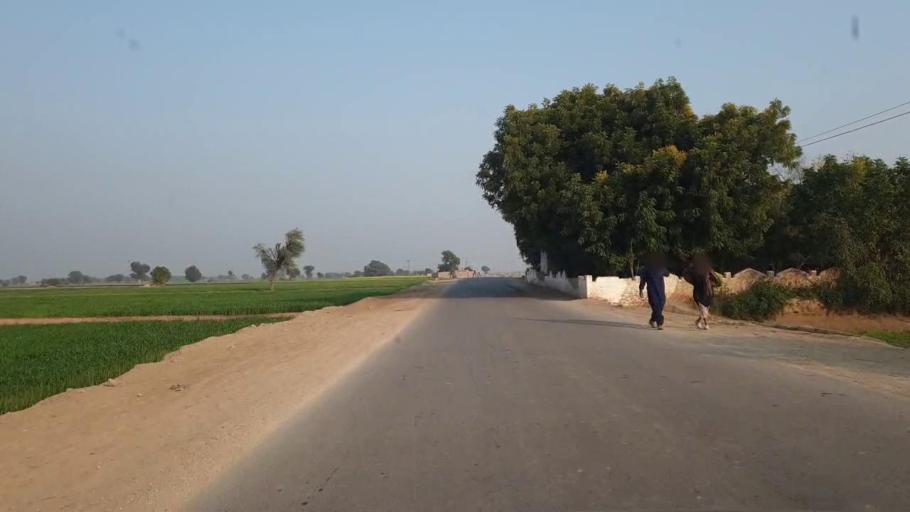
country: PK
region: Sindh
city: Bhit Shah
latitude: 25.8092
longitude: 68.4603
